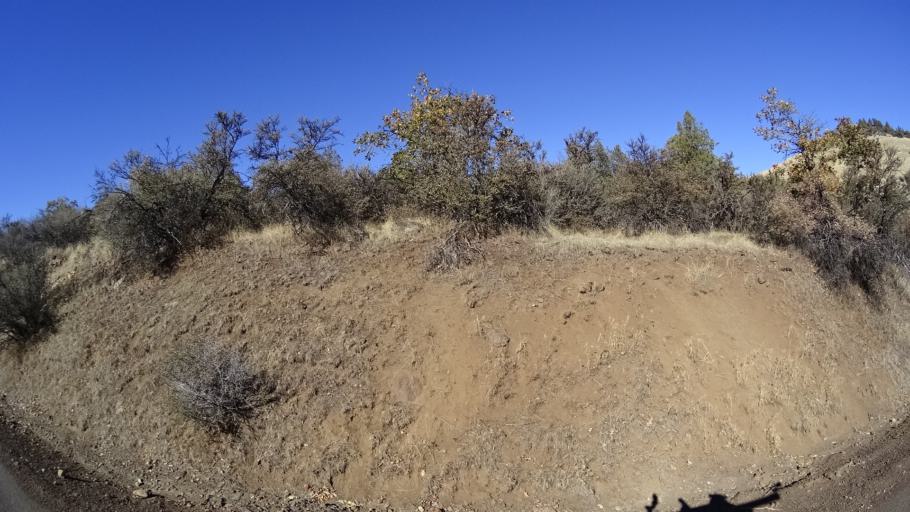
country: US
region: California
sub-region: Siskiyou County
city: Montague
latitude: 41.9554
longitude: -122.3279
